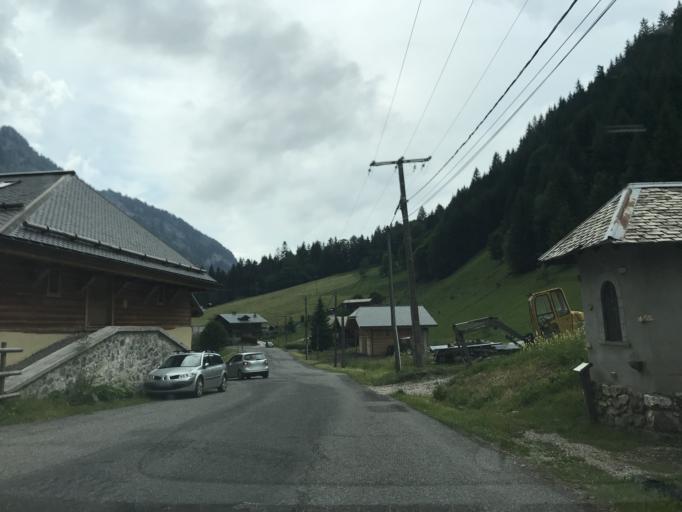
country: FR
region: Rhone-Alpes
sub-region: Departement de la Haute-Savoie
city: Morzine
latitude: 46.1501
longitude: 6.7513
